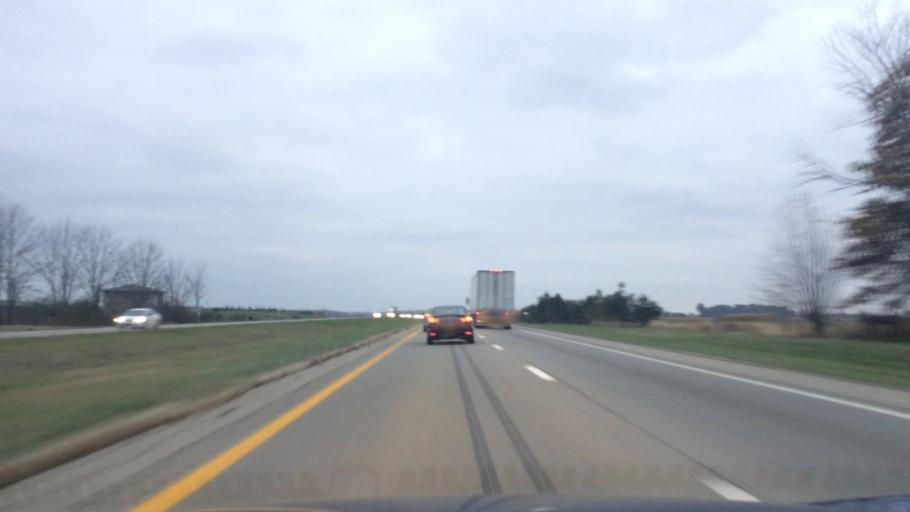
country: US
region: Ohio
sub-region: Union County
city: New California
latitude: 40.1963
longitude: -83.2757
